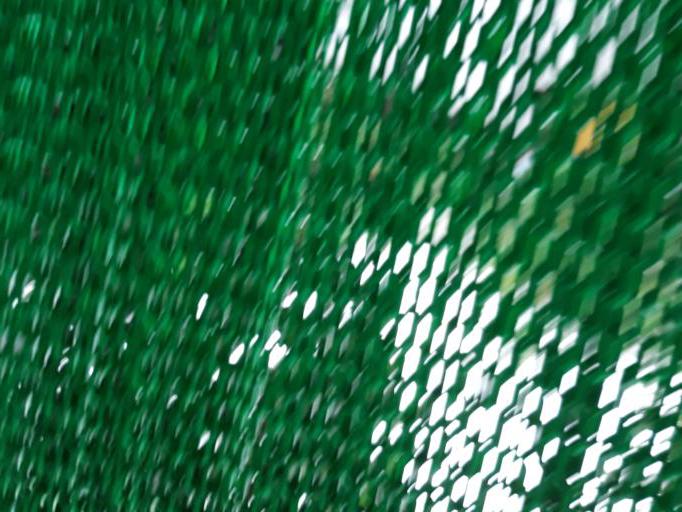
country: TW
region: Taipei
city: Taipei
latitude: 24.9958
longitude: 121.5897
